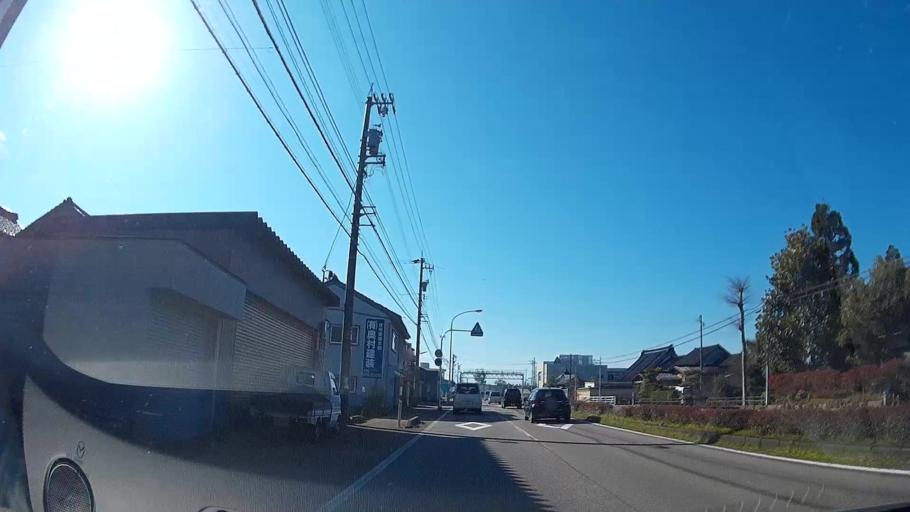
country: JP
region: Toyama
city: Takaoka
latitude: 36.6975
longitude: 136.9840
